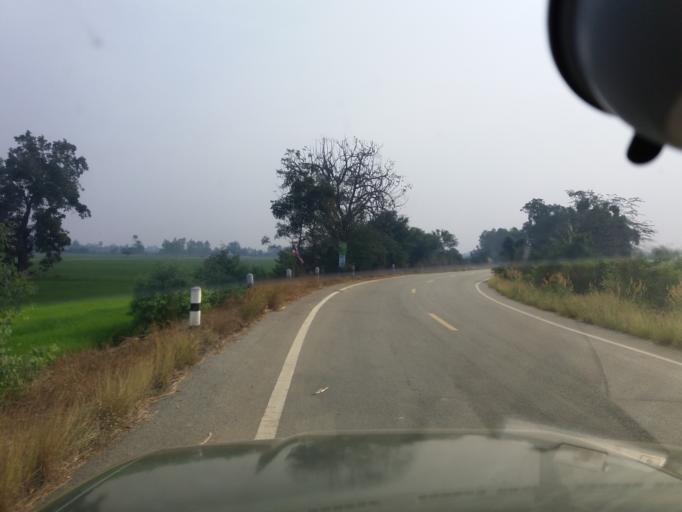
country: TH
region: Suphan Buri
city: Doem Bang Nang Buat
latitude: 14.8558
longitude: 100.1537
